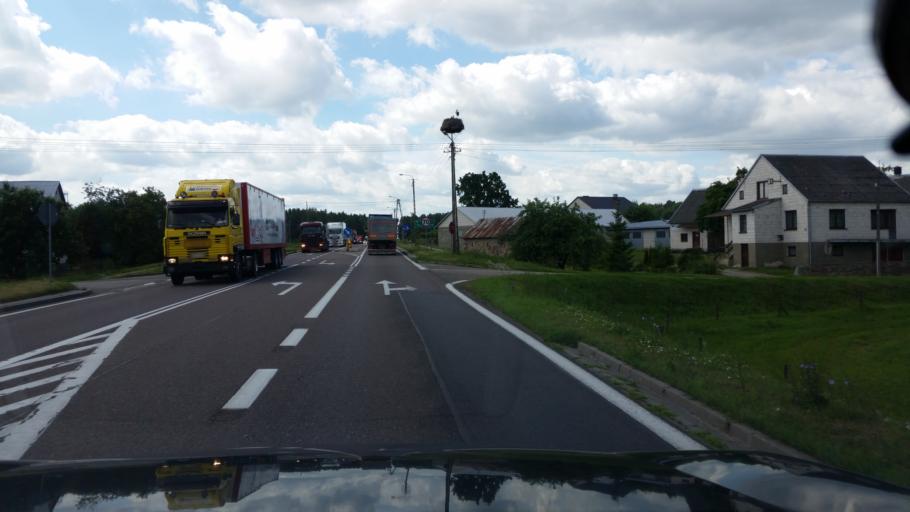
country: PL
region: Podlasie
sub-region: Powiat grajewski
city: Szczuczyn
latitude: 53.5266
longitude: 22.2555
